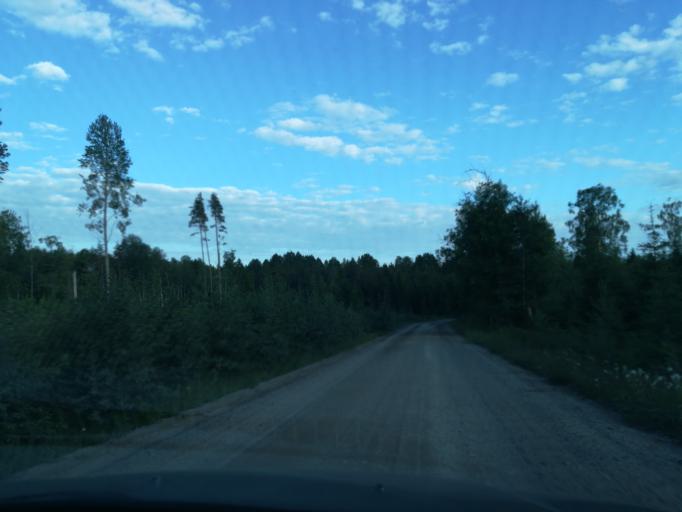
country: FI
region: Southern Savonia
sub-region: Mikkeli
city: Puumala
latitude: 61.6137
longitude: 28.1149
